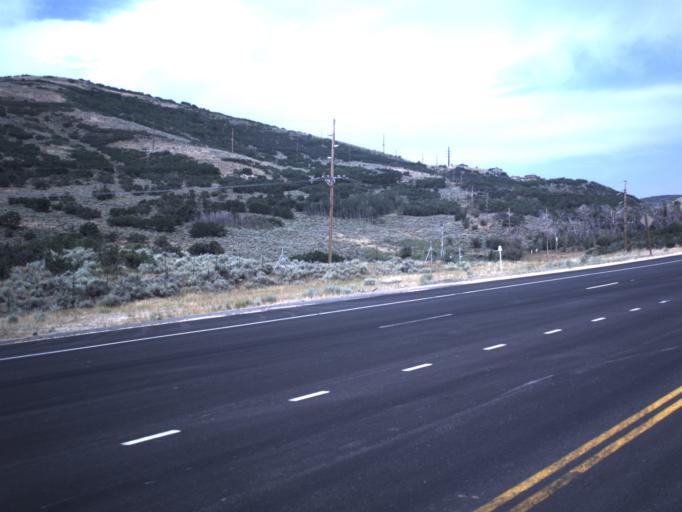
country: US
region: Utah
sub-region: Summit County
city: Park City
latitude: 40.6628
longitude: -111.4169
